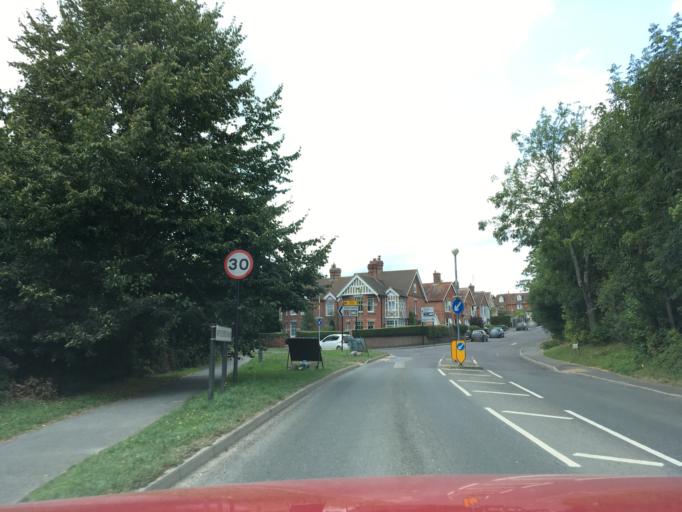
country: GB
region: England
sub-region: Kent
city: Tenterden
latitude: 51.0708
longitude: 0.6973
